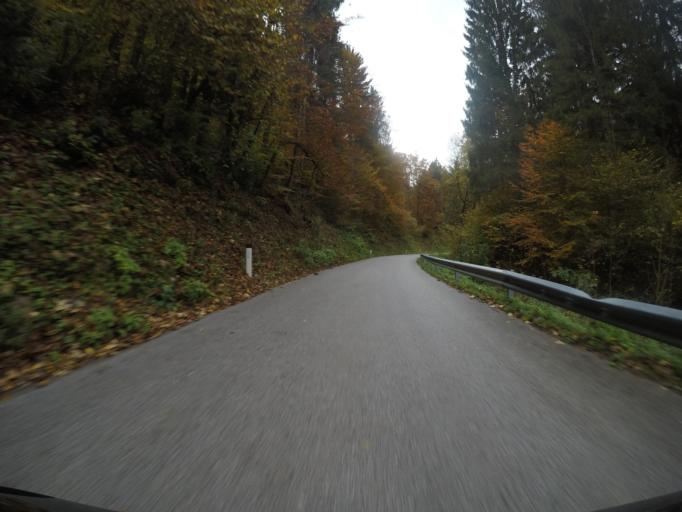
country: SI
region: Gorje
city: Zgornje Gorje
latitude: 46.3882
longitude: 14.0279
